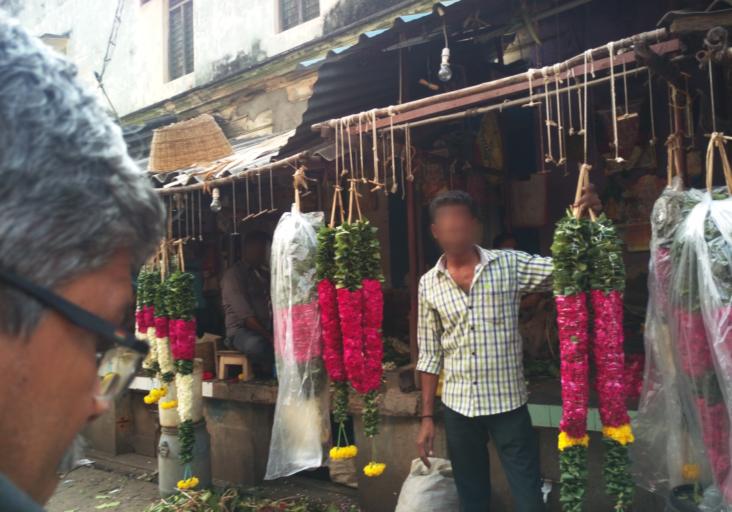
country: IN
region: Andhra Pradesh
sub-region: Chittoor
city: Chittoor
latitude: 13.2172
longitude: 79.0996
